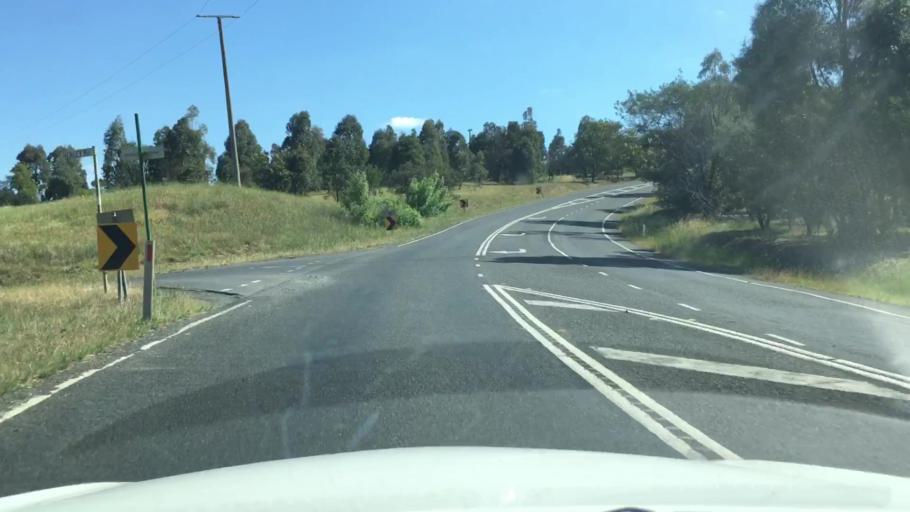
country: AU
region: Victoria
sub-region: Nillumbik
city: North Warrandyte
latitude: -37.6887
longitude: 145.2343
